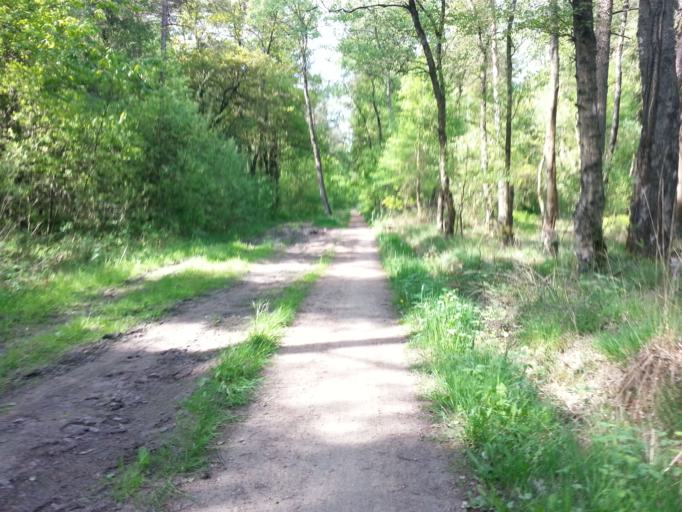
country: NL
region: Overijssel
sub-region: Gemeente Haaksbergen
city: Haaksbergen
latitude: 52.1248
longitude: 6.7043
